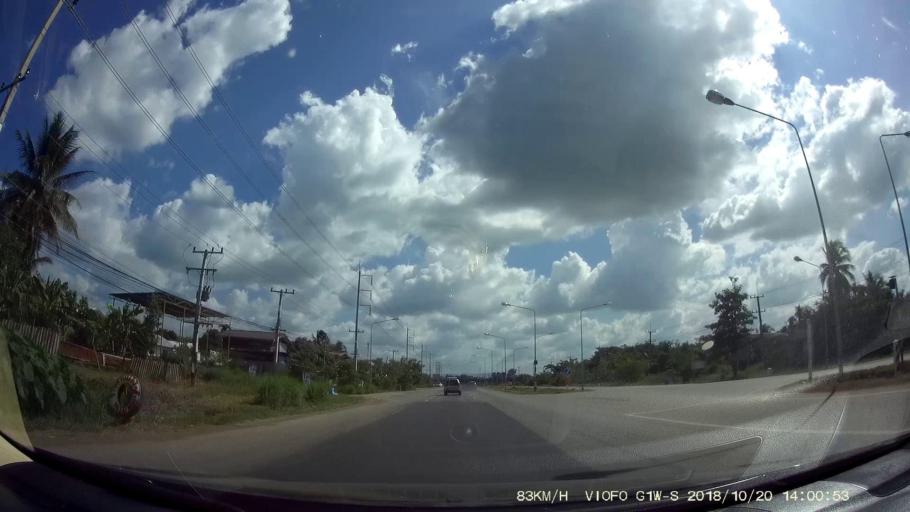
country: TH
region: Khon Kaen
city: Chum Phae
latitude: 16.5087
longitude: 102.1187
